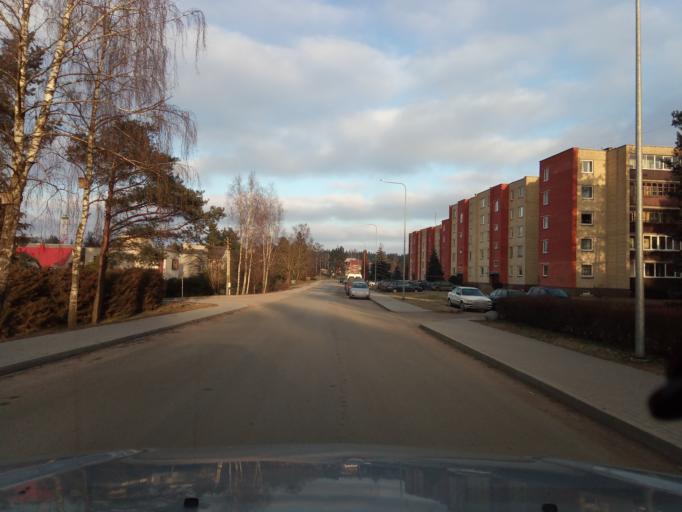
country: LT
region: Alytaus apskritis
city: Varena
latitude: 54.2161
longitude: 24.5595
